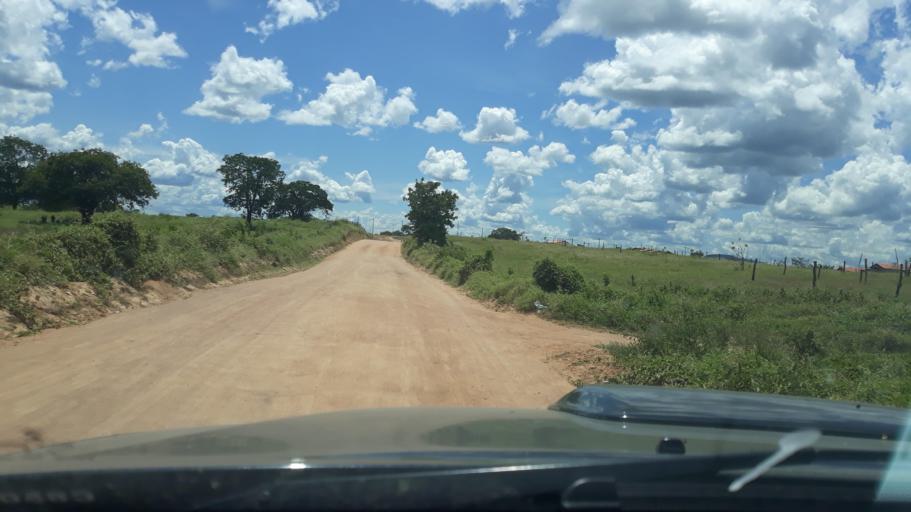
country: BR
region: Bahia
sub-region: Riacho De Santana
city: Riacho de Santana
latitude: -13.9076
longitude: -42.8537
